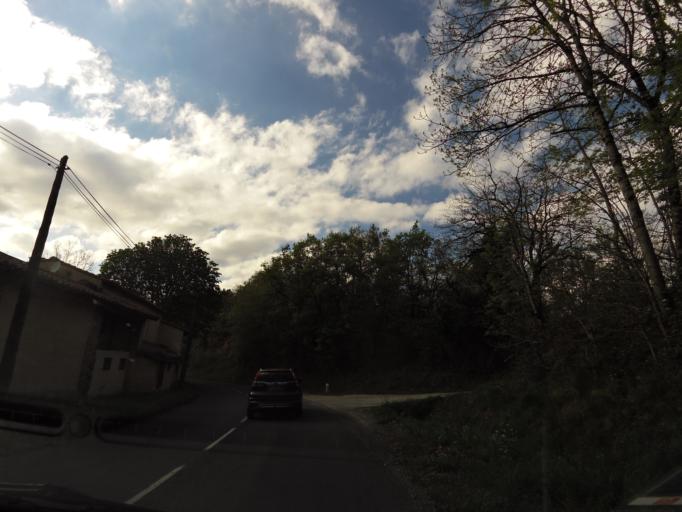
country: FR
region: Midi-Pyrenees
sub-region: Departement du Tarn
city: Soreze
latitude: 43.4347
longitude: 2.0479
